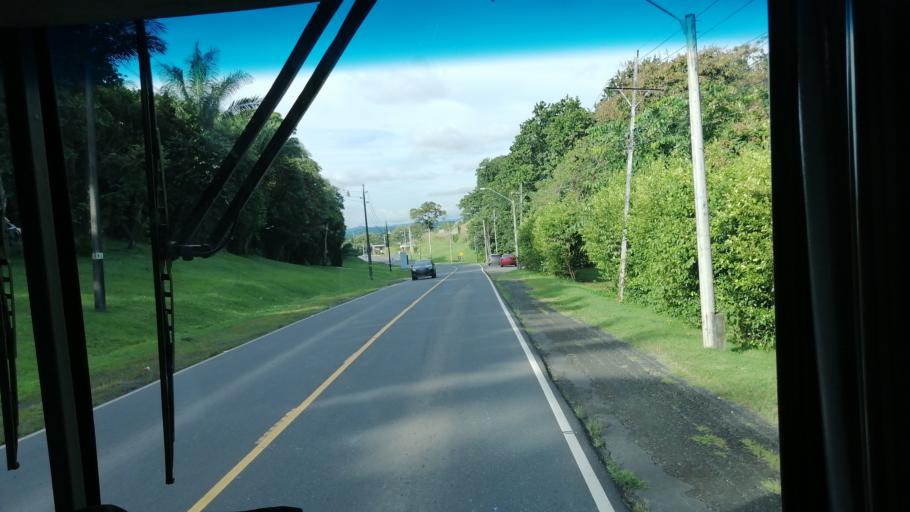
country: PA
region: Panama
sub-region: Distrito de Panama
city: Ancon
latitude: 8.9464
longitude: -79.5911
